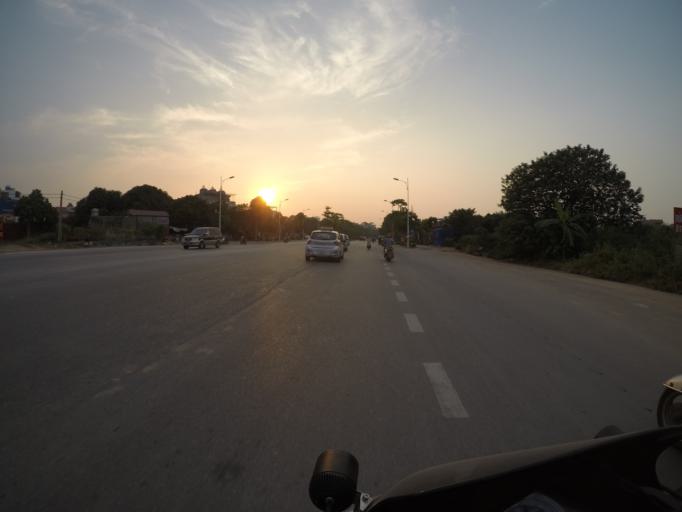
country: VN
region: Ha Noi
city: Hoan Kiem
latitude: 21.0291
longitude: 105.8877
